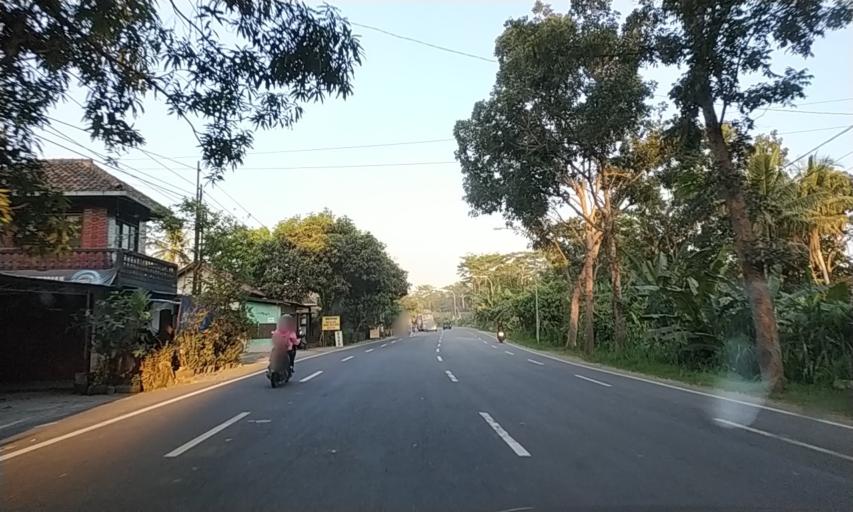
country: ID
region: Daerah Istimewa Yogyakarta
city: Srandakan
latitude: -7.8862
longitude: 110.0523
